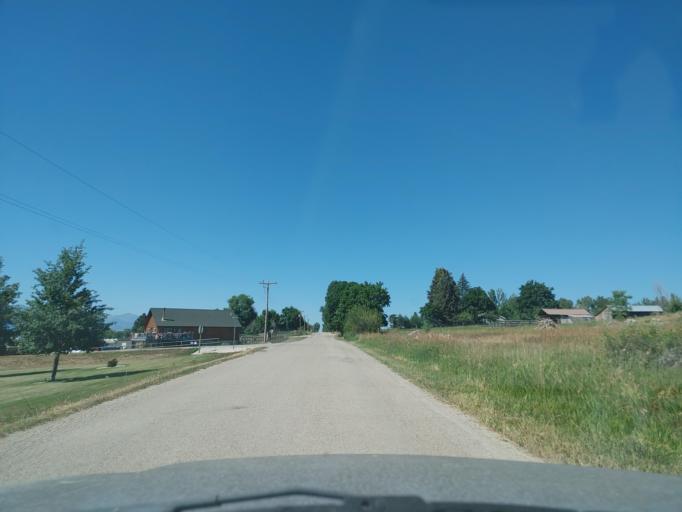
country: US
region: Montana
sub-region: Ravalli County
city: Hamilton
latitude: 46.3238
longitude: -114.0613
